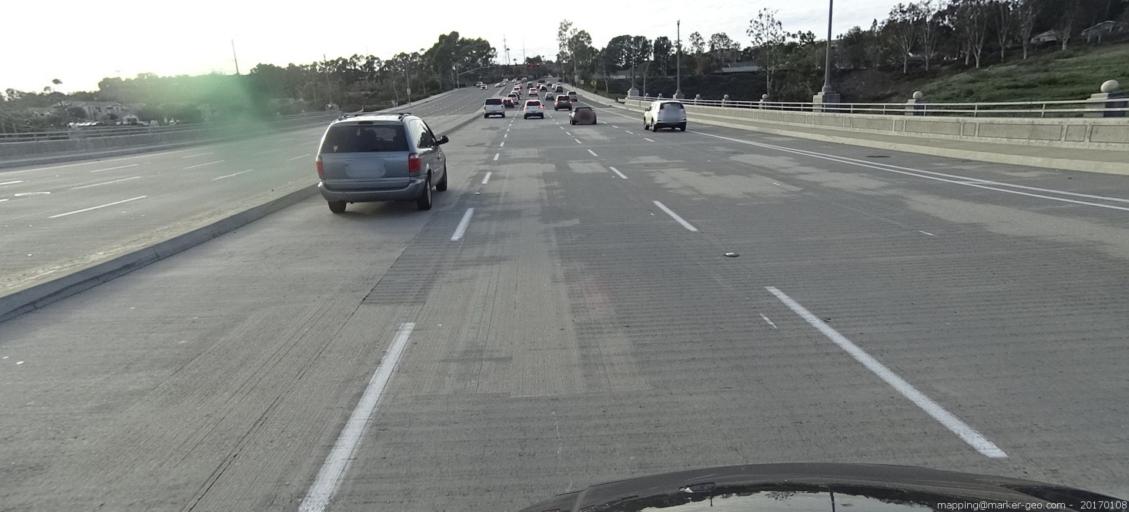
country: US
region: California
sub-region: Orange County
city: Ladera Ranch
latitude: 33.5630
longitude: -117.6517
